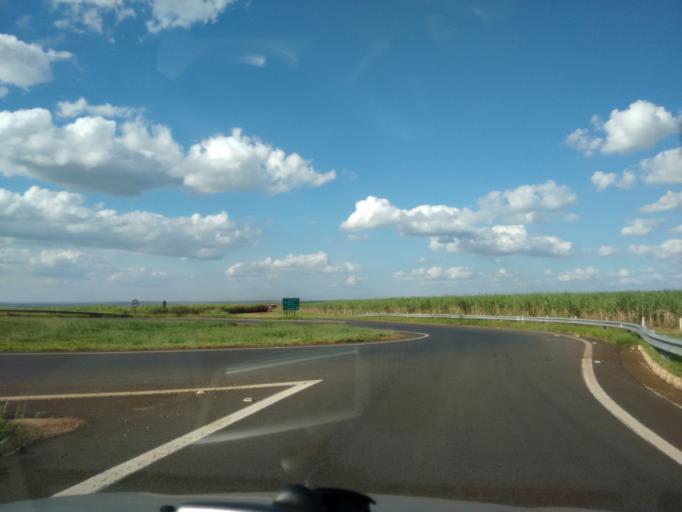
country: BR
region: Sao Paulo
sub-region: Americo Brasiliense
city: Americo Brasiliense
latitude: -21.6245
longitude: -47.9642
